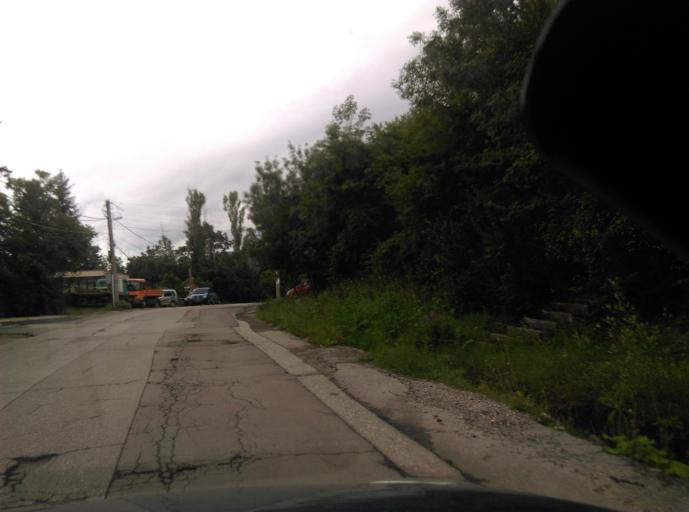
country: BG
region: Sofia-Capital
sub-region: Stolichna Obshtina
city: Sofia
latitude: 42.6376
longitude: 23.2975
